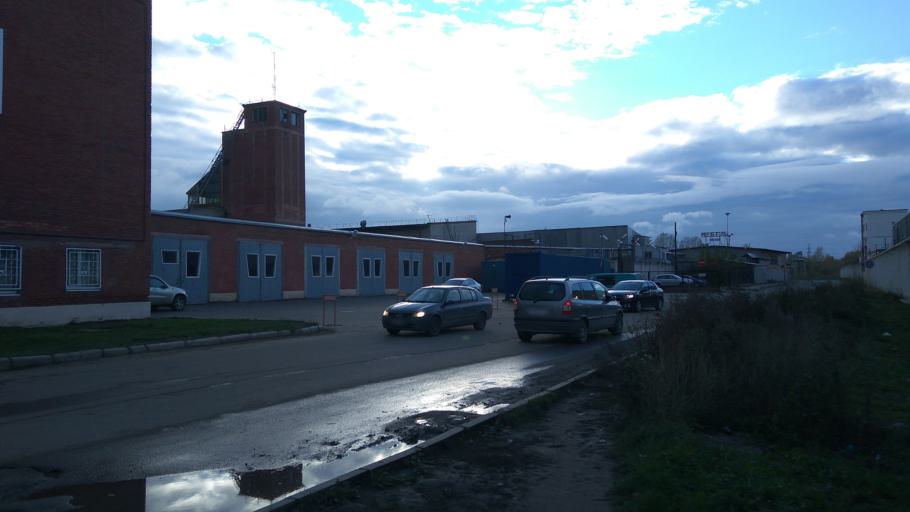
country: RU
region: Tatarstan
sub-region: Gorod Kazan'
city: Kazan
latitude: 55.7334
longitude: 49.1339
